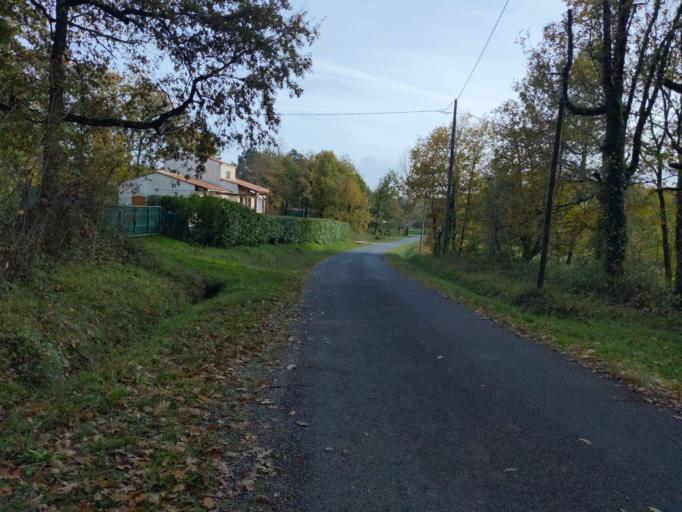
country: FR
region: Aquitaine
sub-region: Departement du Lot-et-Garonne
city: Fumel
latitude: 44.5474
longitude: 0.9387
